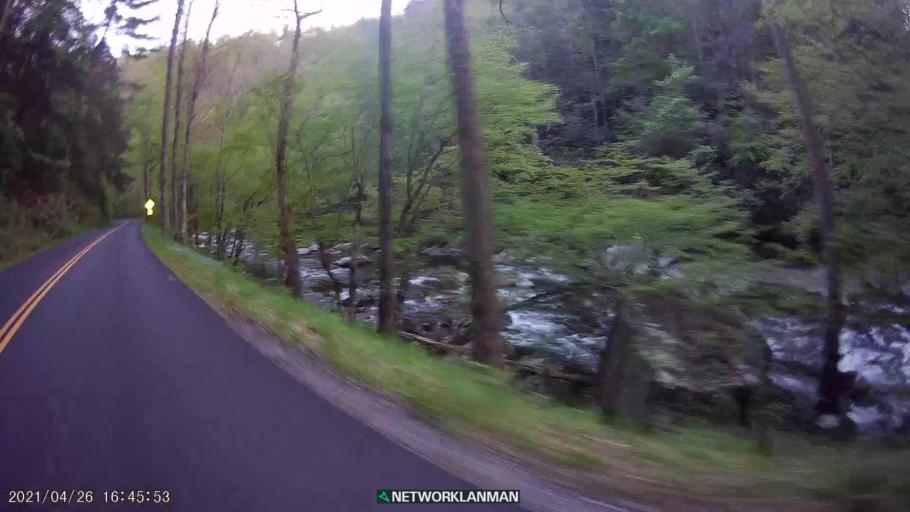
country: US
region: Tennessee
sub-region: Sevier County
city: Gatlinburg
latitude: 35.6678
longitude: -83.6681
